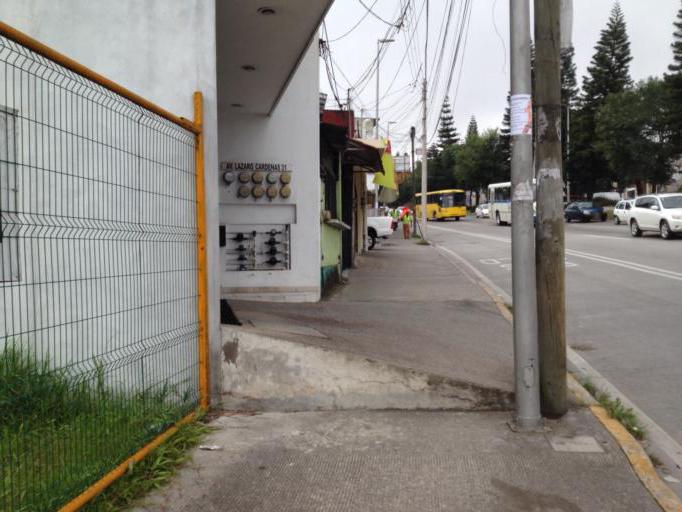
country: MX
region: Veracruz
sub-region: Xalapa
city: Xalapa de Enriquez
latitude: 19.5289
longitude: -96.8991
